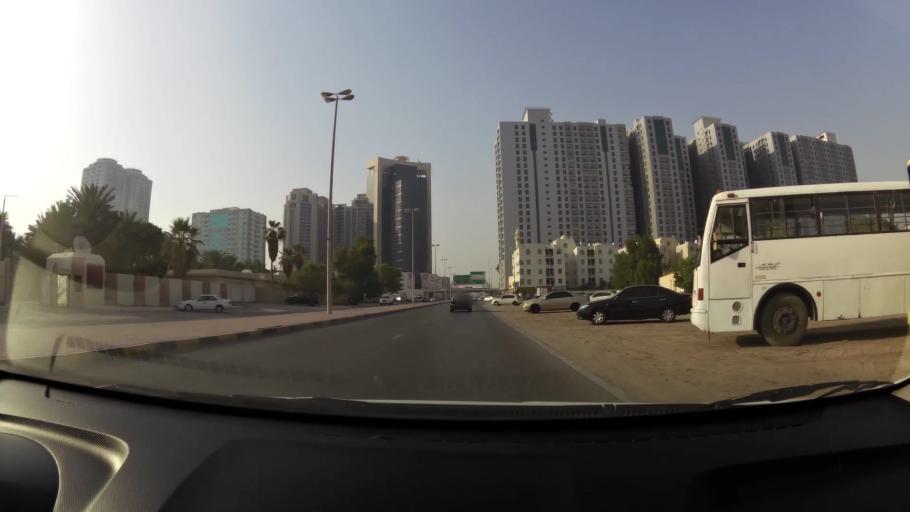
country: AE
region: Ajman
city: Ajman
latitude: 25.3888
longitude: 55.4396
